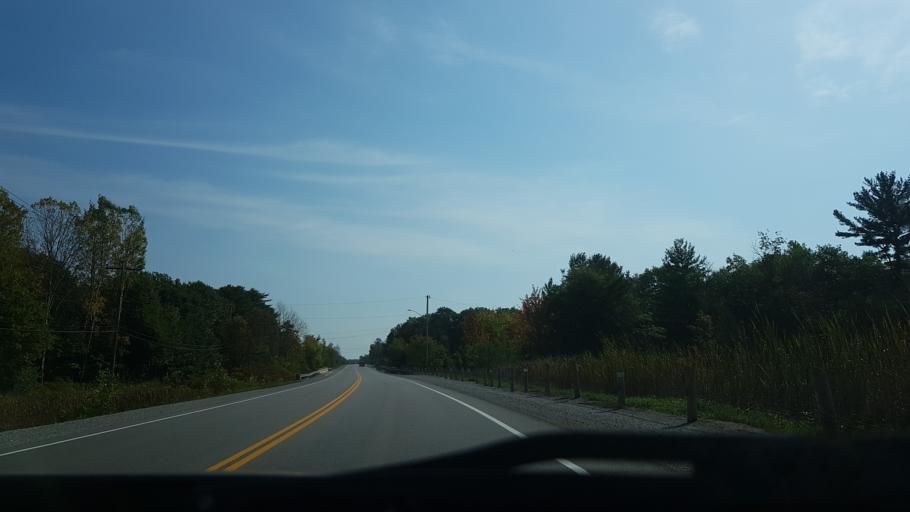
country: CA
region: Ontario
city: Orillia
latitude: 44.7439
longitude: -79.3162
